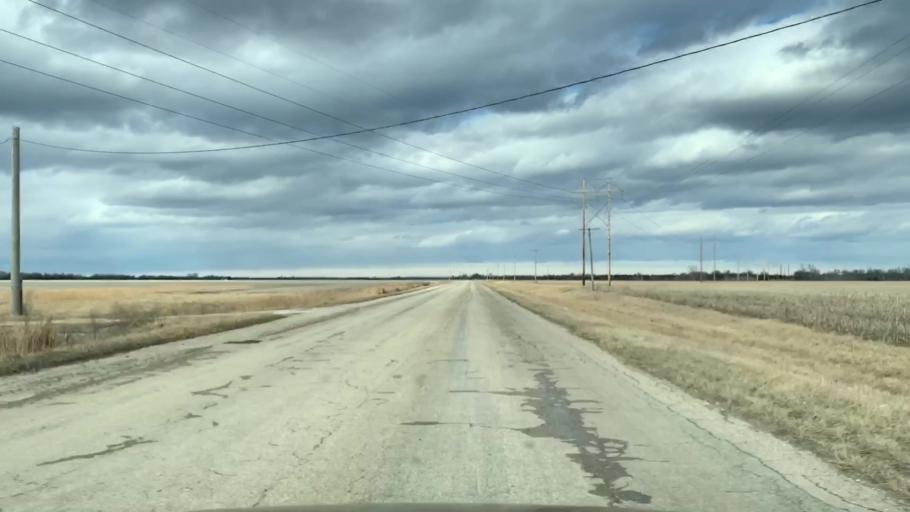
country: US
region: Kansas
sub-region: Allen County
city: Humboldt
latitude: 37.7696
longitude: -95.4706
